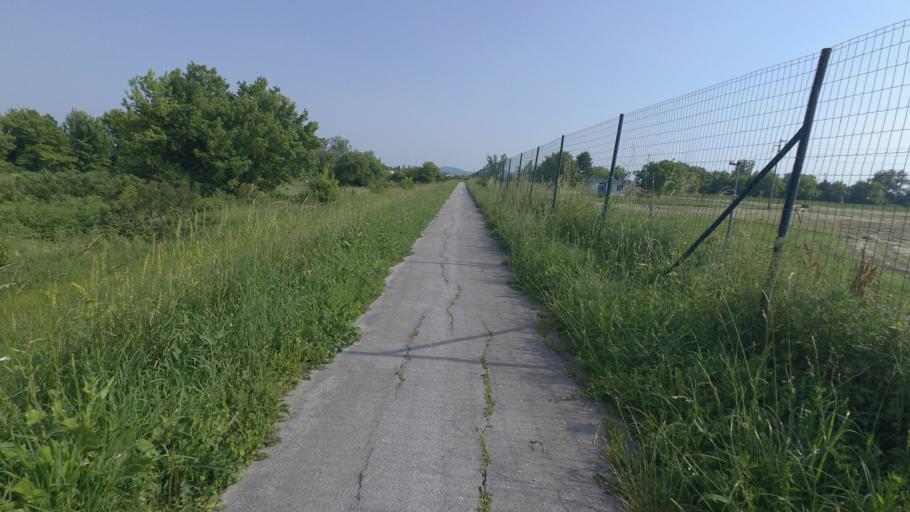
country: HR
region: Karlovacka
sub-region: Grad Karlovac
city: Karlovac
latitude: 45.4918
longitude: 15.5710
